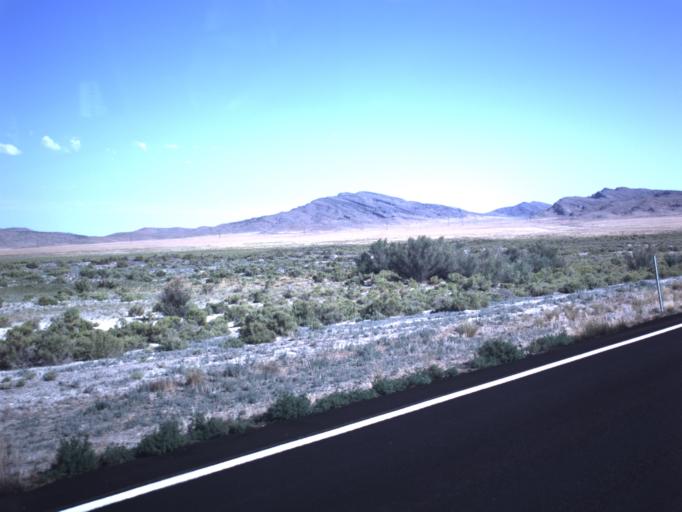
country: US
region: Utah
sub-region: Beaver County
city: Milford
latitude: 38.7199
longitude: -112.9685
